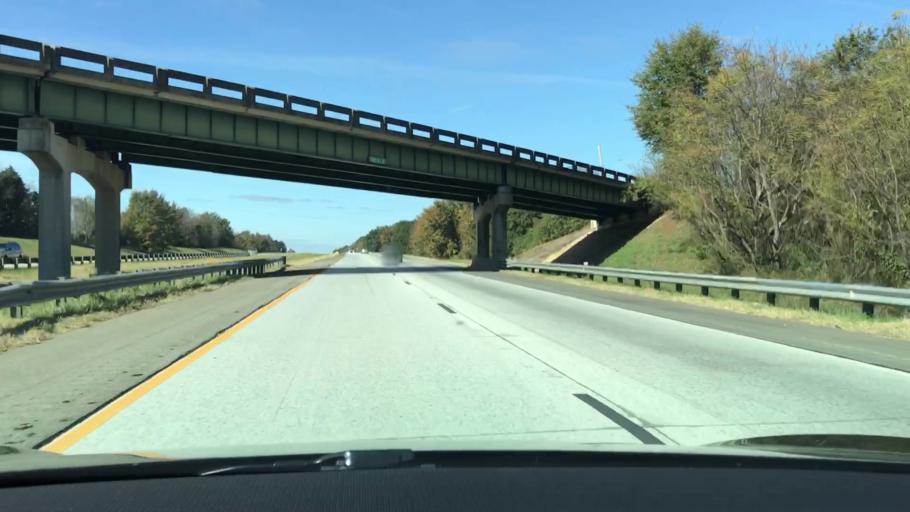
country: US
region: Georgia
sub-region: Putnam County
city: Jefferson
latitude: 33.5400
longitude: -83.3149
